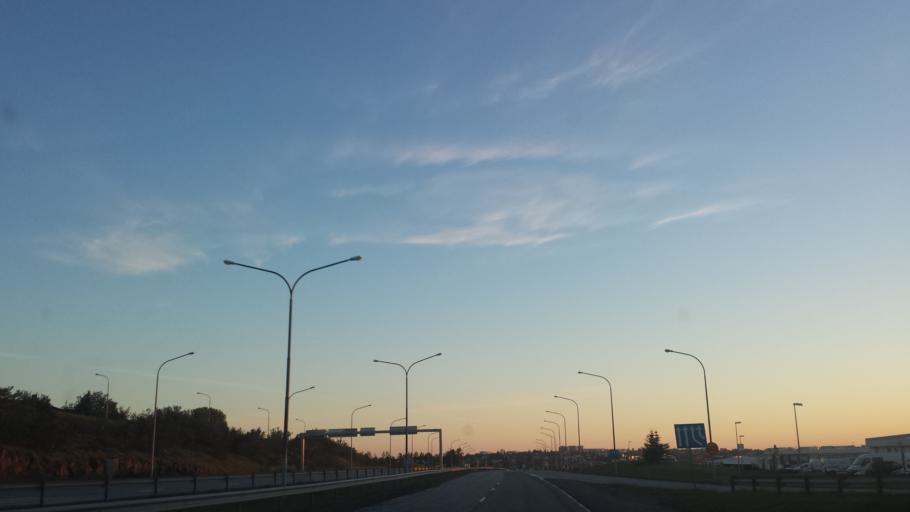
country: IS
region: Capital Region
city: Reykjavik
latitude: 64.1242
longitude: -21.8142
